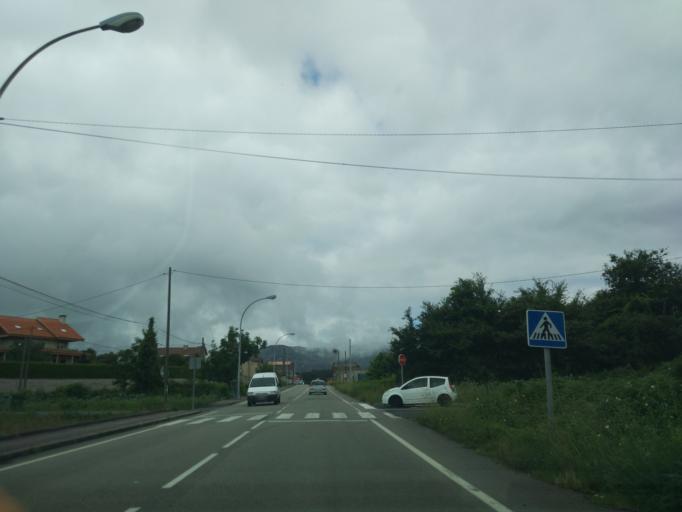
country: ES
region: Galicia
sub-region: Provincia da Coruna
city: Boiro
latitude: 42.6441
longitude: -8.8711
